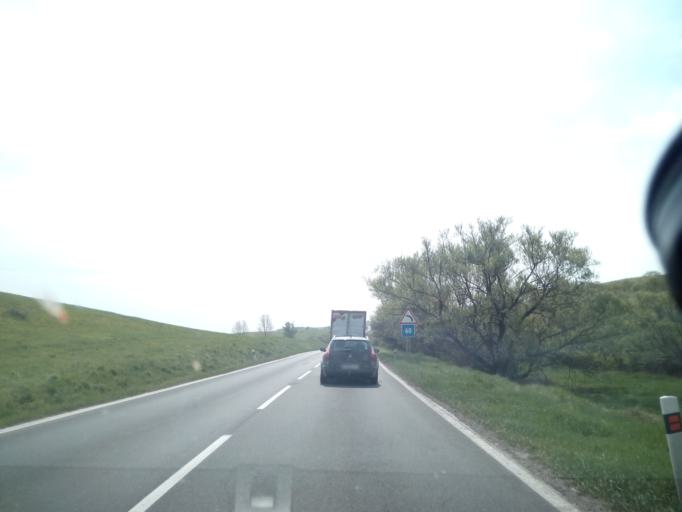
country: SK
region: Presovsky
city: Giraltovce
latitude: 49.0426
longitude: 21.4448
